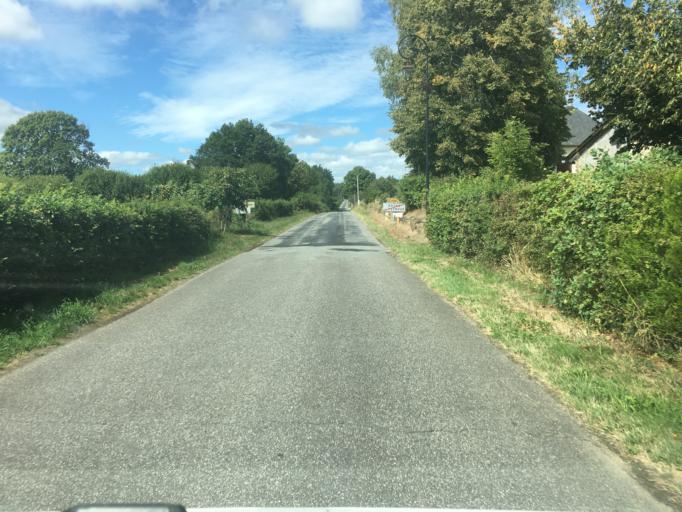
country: FR
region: Auvergne
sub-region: Departement du Cantal
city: Champagnac
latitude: 45.4235
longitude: 2.3788
